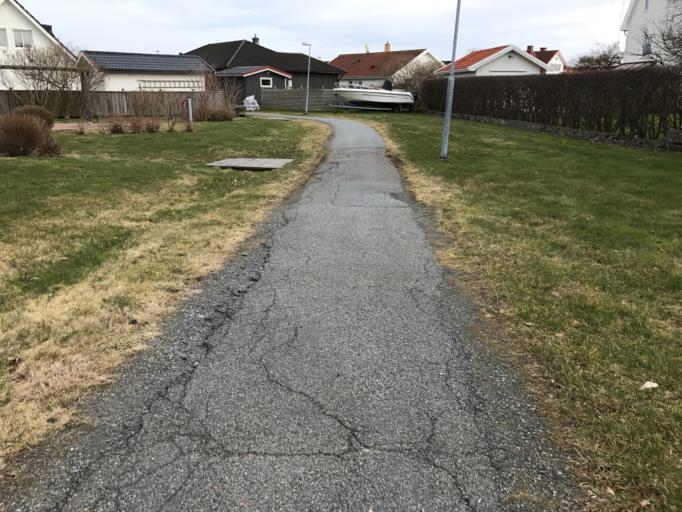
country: SE
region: Vaestra Goetaland
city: Donso
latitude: 57.5723
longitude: 11.7827
